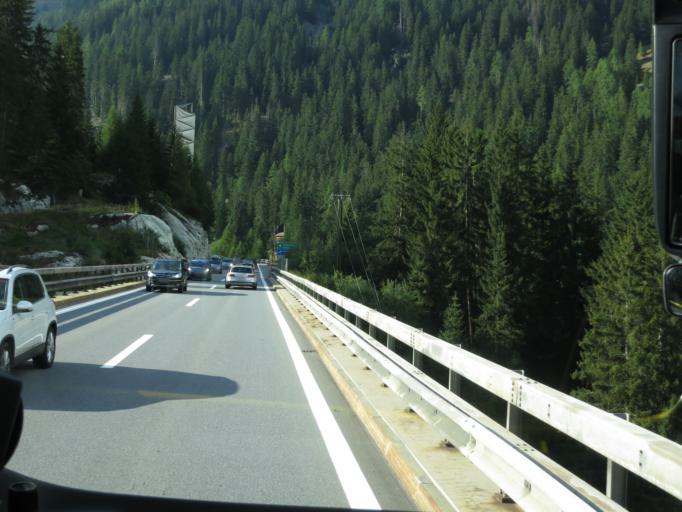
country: CH
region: Grisons
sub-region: Hinterrhein District
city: Thusis
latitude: 46.5676
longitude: 9.3824
